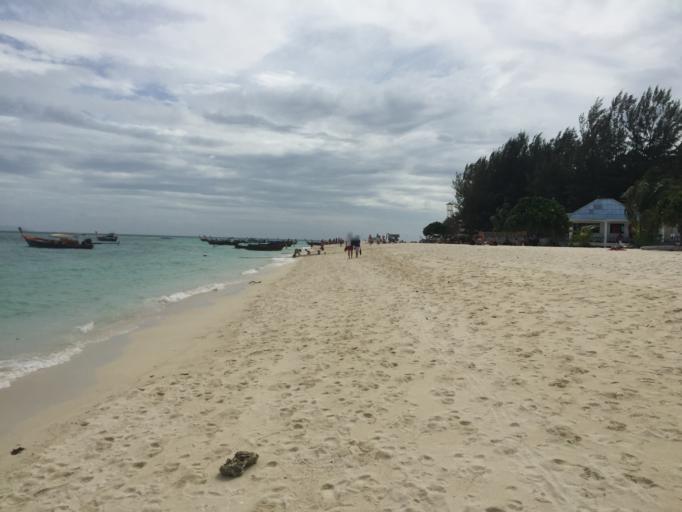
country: MY
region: Kedah
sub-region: Langkawi
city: Kuah
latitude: 6.4939
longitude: 99.3085
